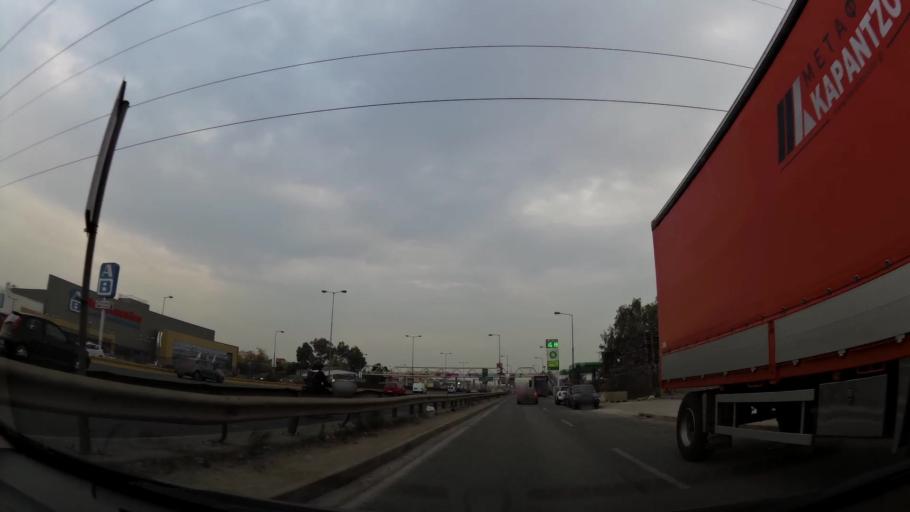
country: GR
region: Attica
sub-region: Nomarchia Athinas
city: Aigaleo
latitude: 37.9818
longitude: 23.6813
